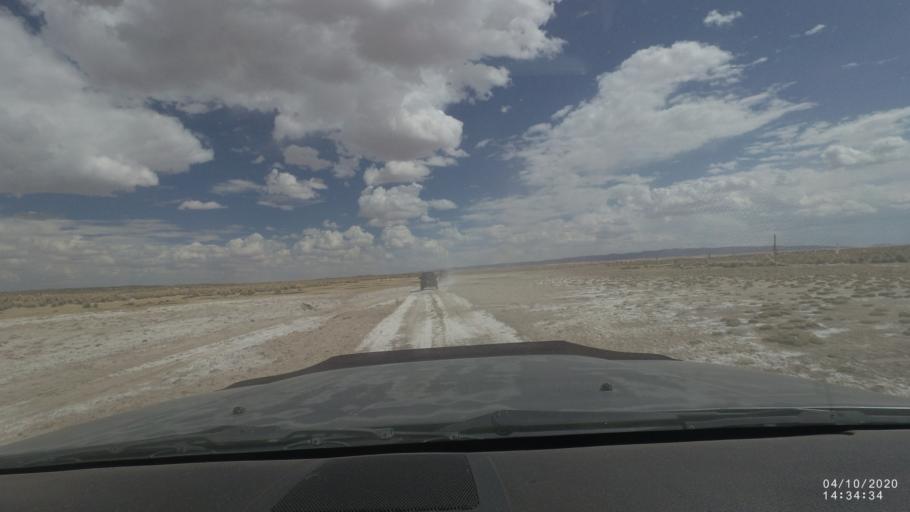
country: BO
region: Oruro
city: Poopo
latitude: -18.6715
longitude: -67.4695
